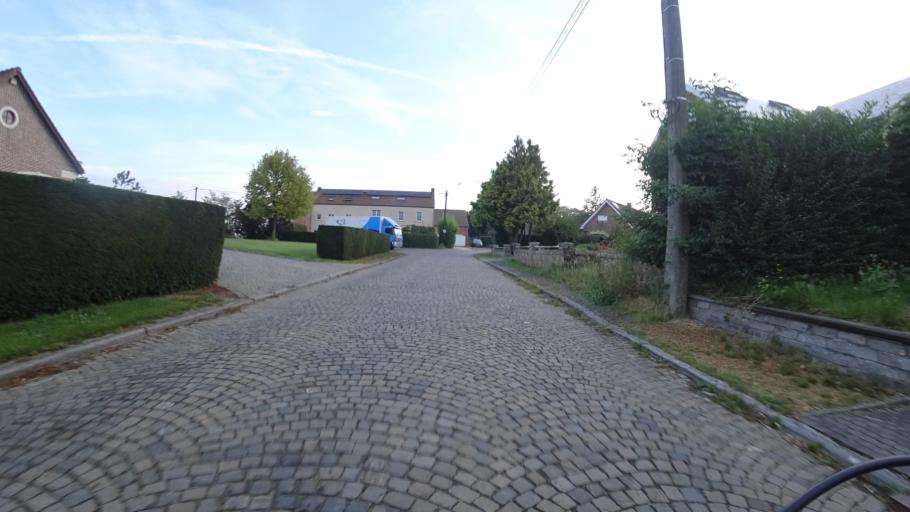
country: BE
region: Wallonia
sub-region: Province du Brabant Wallon
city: Perwez
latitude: 50.5863
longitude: 4.7679
